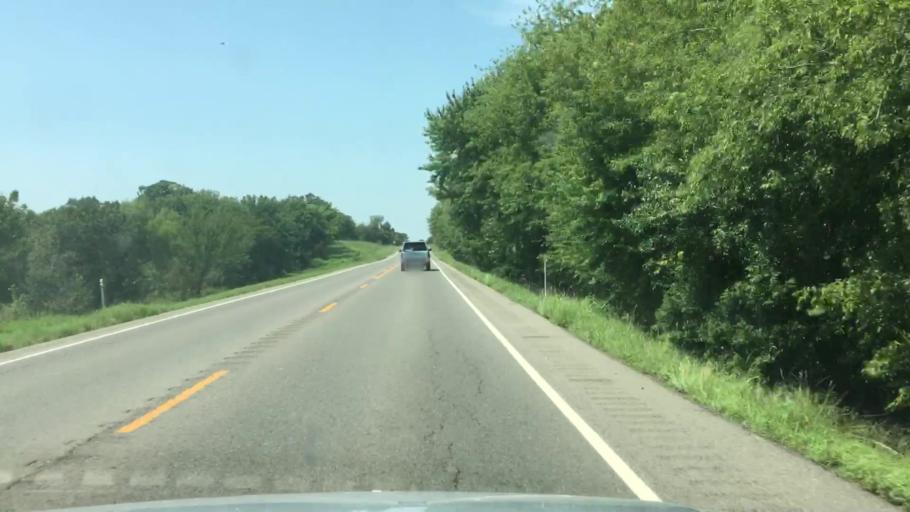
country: US
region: Oklahoma
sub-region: Wagoner County
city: Wagoner
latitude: 35.9371
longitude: -95.3363
